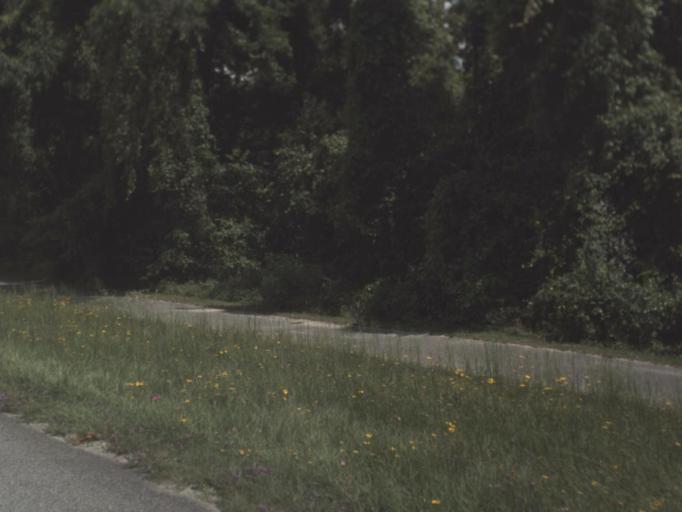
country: US
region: Florida
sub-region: Alachua County
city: High Springs
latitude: 29.9481
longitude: -82.7495
